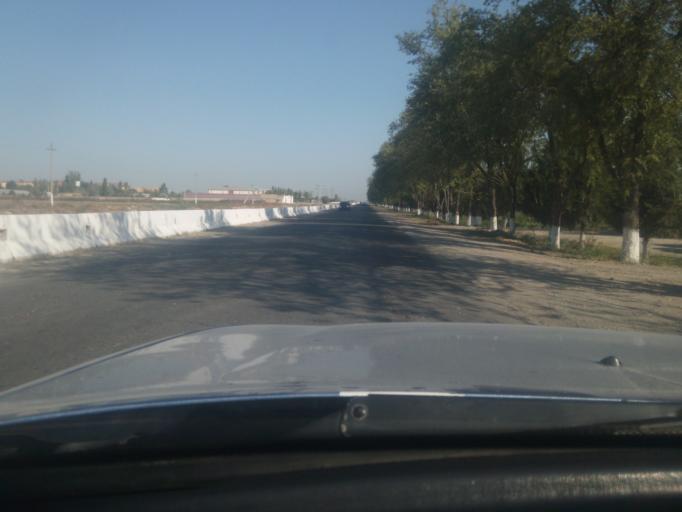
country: UZ
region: Sirdaryo
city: Guliston
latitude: 40.5115
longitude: 68.7951
